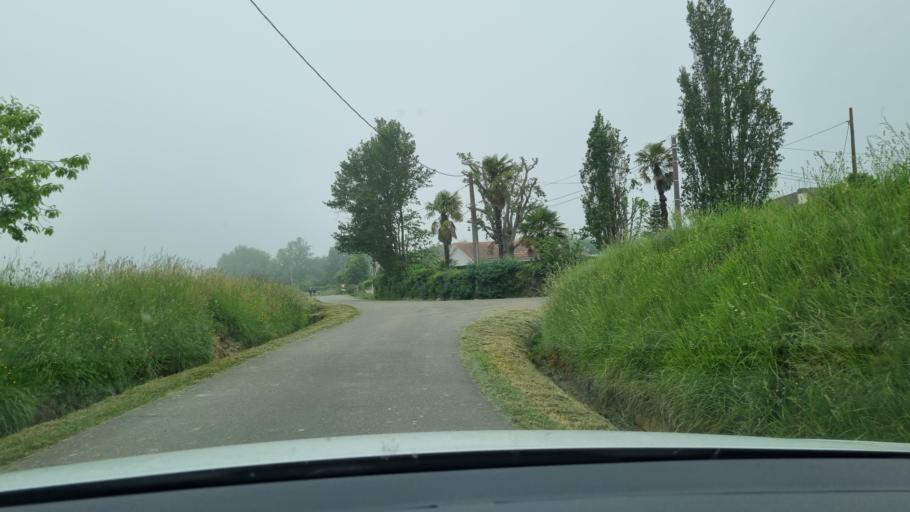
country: FR
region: Aquitaine
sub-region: Departement des Landes
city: Hagetmau
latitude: 43.6488
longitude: -0.6096
